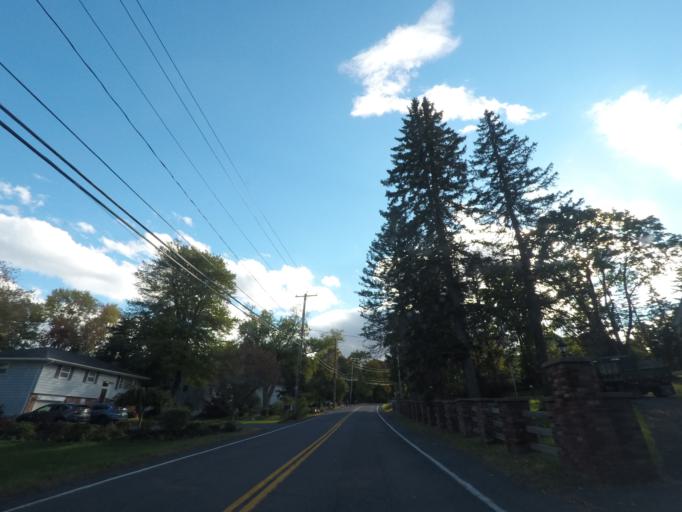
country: US
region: New York
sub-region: Schenectady County
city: Niskayuna
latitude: 42.7716
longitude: -73.8254
